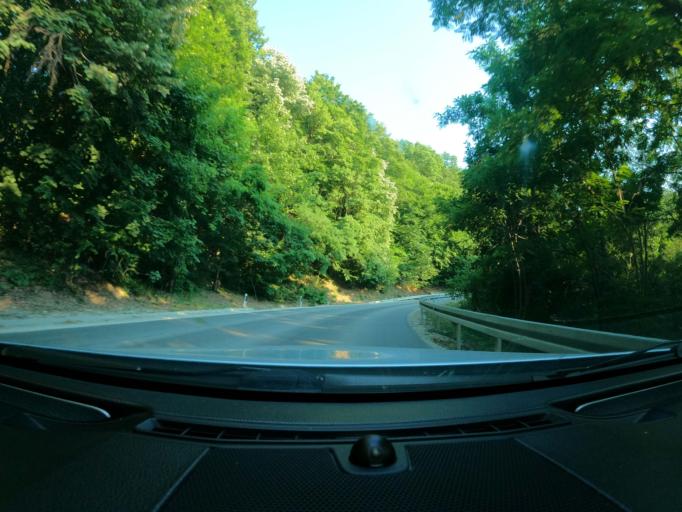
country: RS
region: Autonomna Pokrajina Vojvodina
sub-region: Juznobacki Okrug
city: Beocin
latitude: 45.1584
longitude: 19.7152
